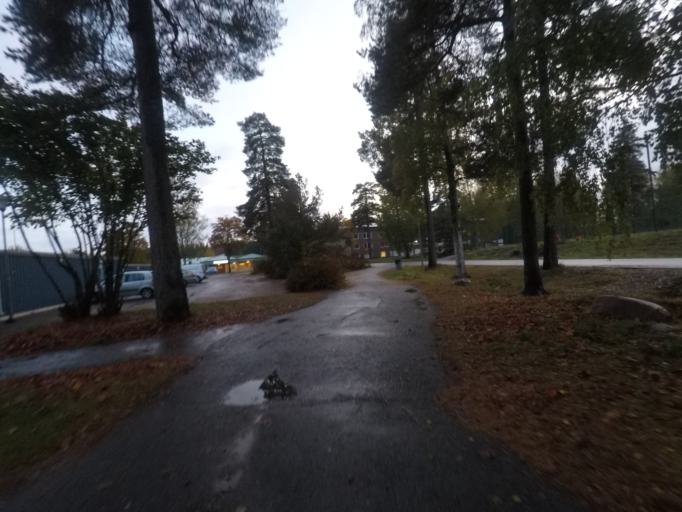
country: SE
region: OErebro
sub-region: Karlskoga Kommun
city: Karlskoga
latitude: 59.3156
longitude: 14.4889
